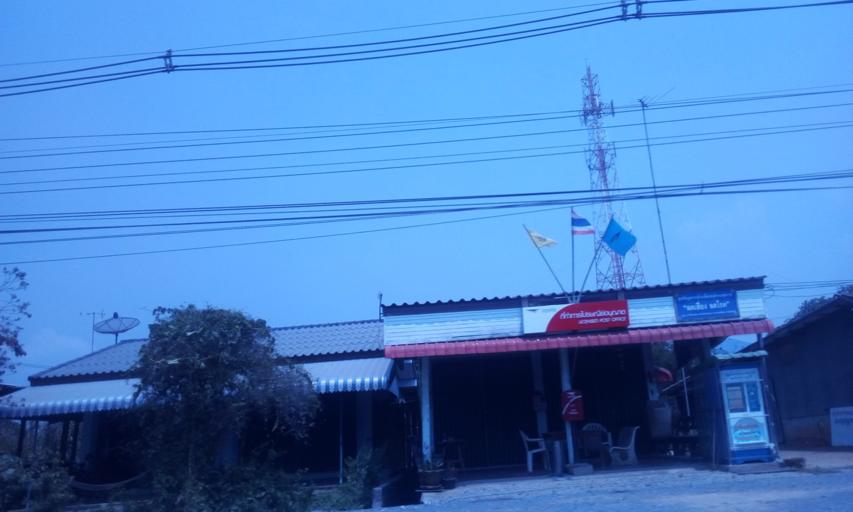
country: TH
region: Chon Buri
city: Phan Thong
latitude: 13.5396
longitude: 101.1473
